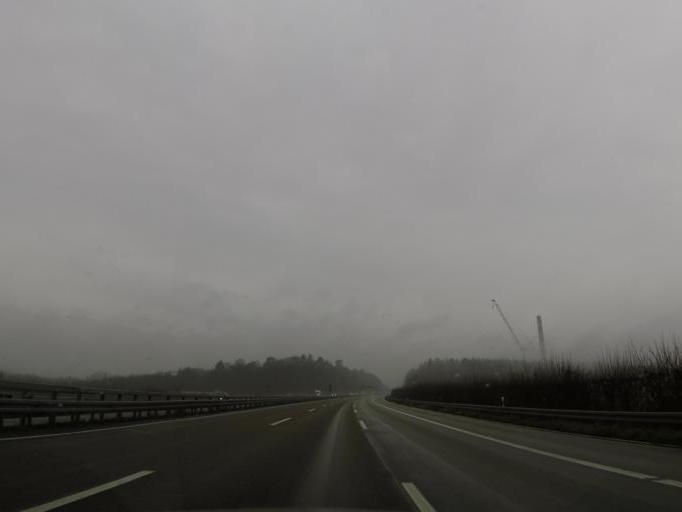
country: DE
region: Rheinland-Pfalz
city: Aull
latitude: 50.4051
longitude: 8.0072
